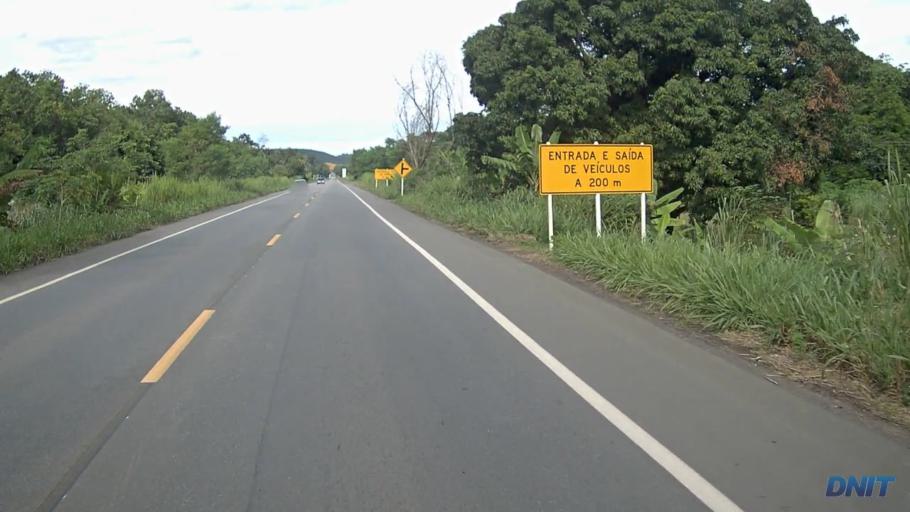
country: BR
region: Minas Gerais
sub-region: Ipaba
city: Ipaba
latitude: -19.2997
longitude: -42.3750
